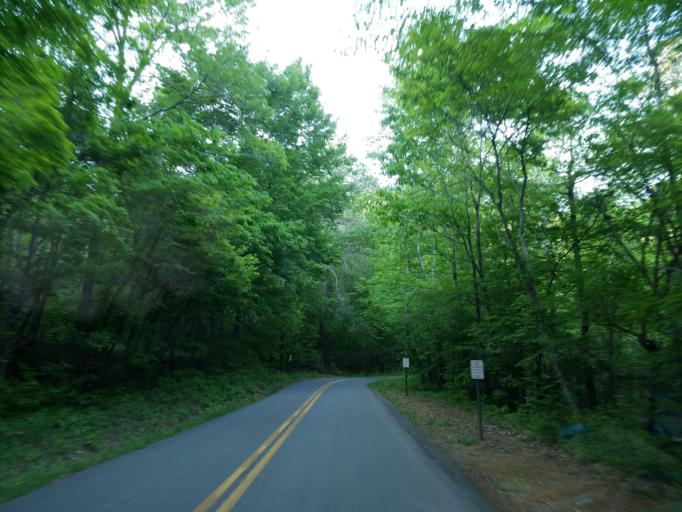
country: US
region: Georgia
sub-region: Gordon County
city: Calhoun
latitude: 34.5789
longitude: -85.0983
